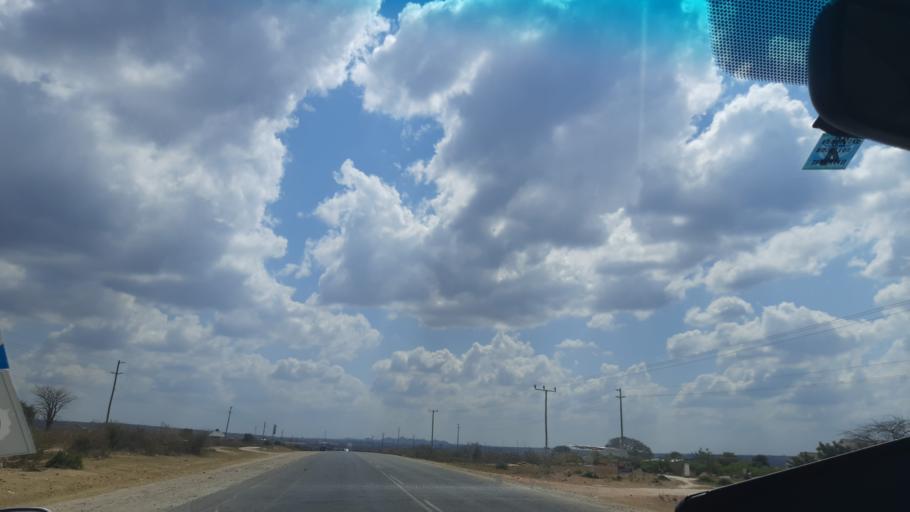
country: TZ
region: Dodoma
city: Dodoma
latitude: -6.1404
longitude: 35.6933
